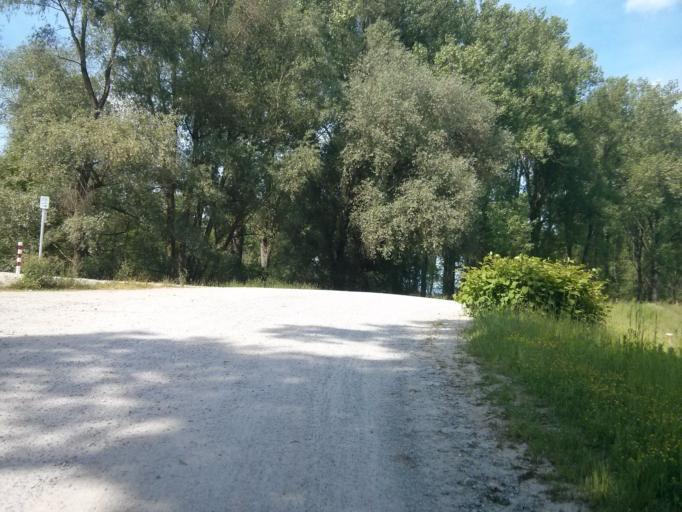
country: DE
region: Bavaria
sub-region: Lower Bavaria
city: Plattling
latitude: 48.7763
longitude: 12.8986
